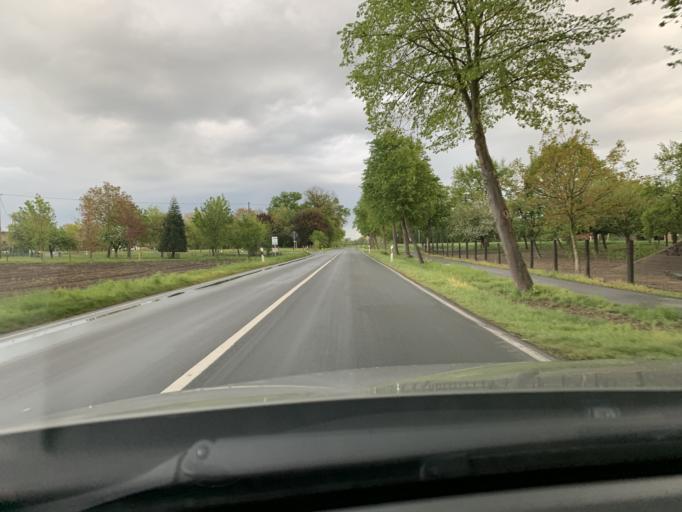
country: DE
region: North Rhine-Westphalia
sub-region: Regierungsbezirk Detmold
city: Langenberg
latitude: 51.7907
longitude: 8.3712
